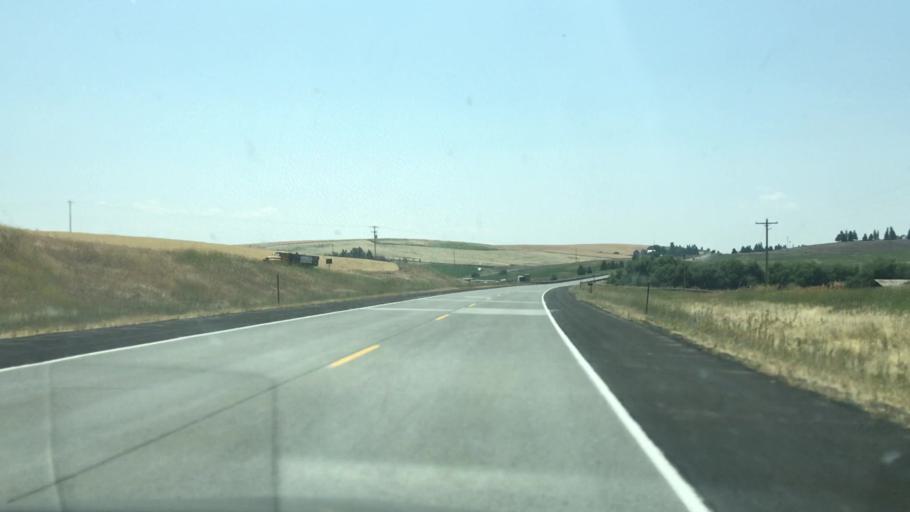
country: US
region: Idaho
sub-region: Lewis County
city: Nezperce
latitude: 46.0723
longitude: -116.3417
